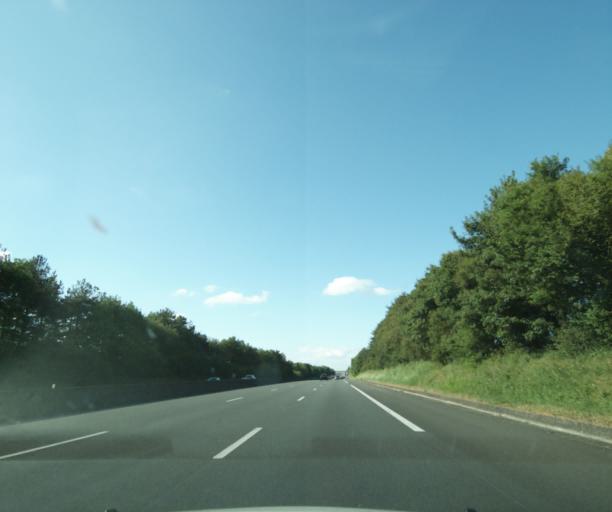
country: FR
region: Centre
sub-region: Departement d'Eure-et-Loir
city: Janville
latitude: 48.1686
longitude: 1.8538
